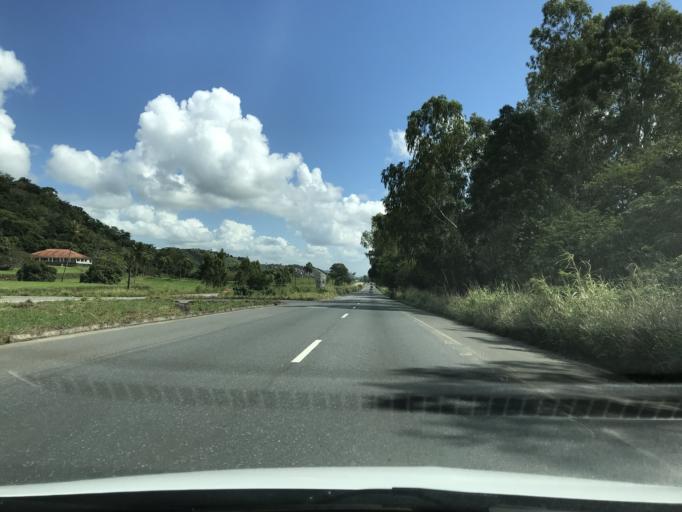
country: BR
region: Pernambuco
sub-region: Moreno
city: Moreno
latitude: -8.1054
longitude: -35.1753
